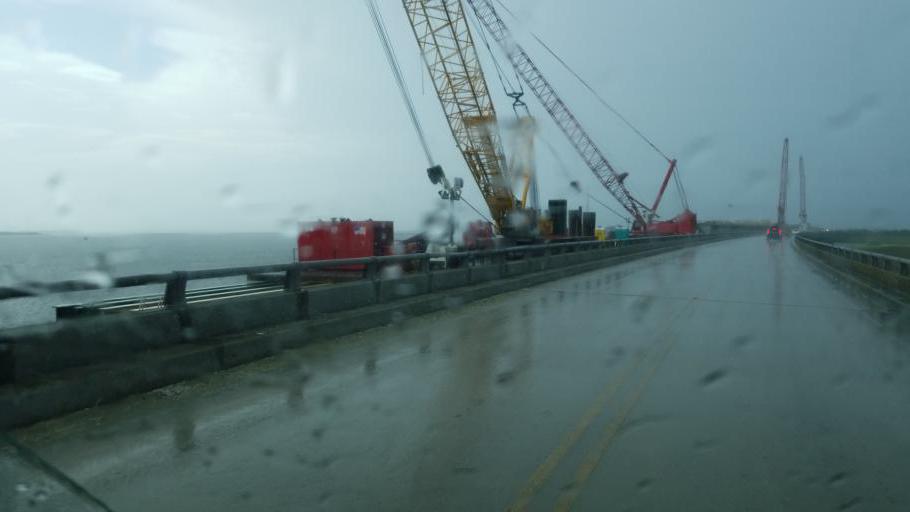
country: US
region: North Carolina
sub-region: Dare County
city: Wanchese
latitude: 35.7859
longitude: -75.5468
